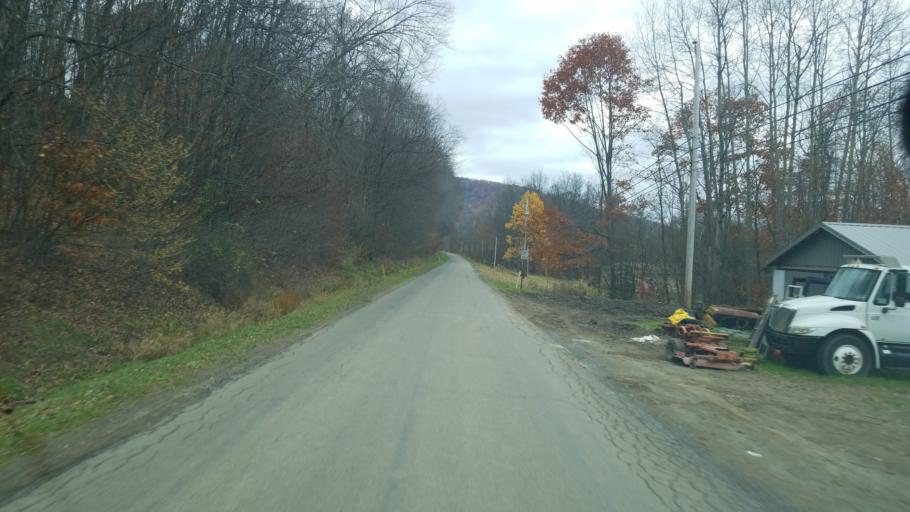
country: US
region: Pennsylvania
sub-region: McKean County
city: Smethport
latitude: 41.7997
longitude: -78.4308
